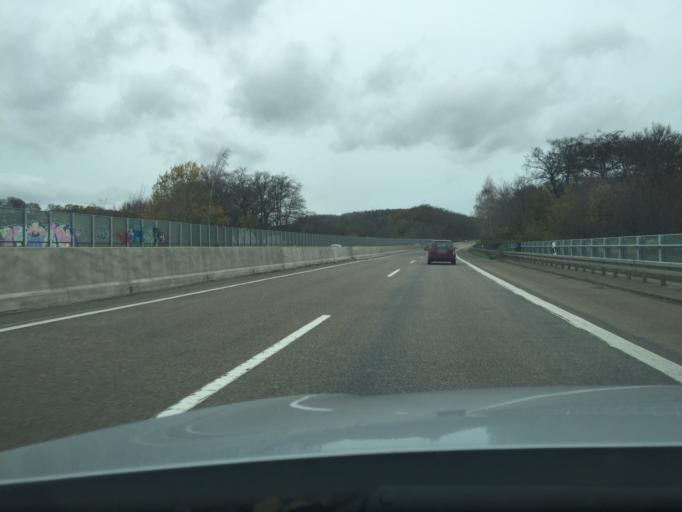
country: DE
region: North Rhine-Westphalia
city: Wulfrath
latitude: 51.2807
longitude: 7.0748
